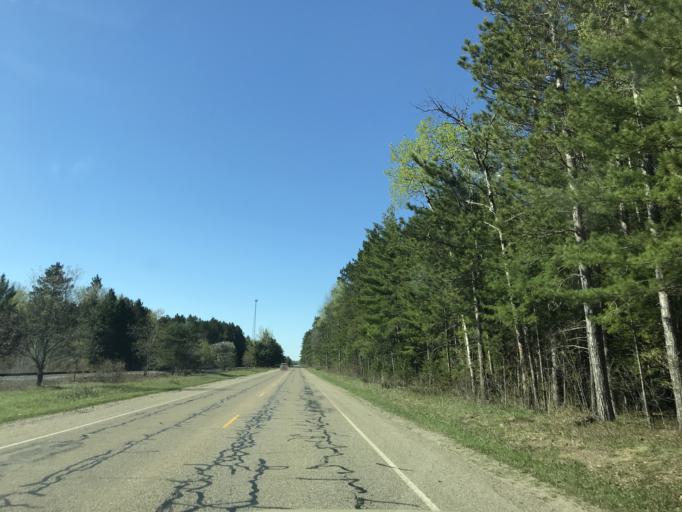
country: US
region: Michigan
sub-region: Crawford County
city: Grayling
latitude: 44.7332
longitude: -84.7490
